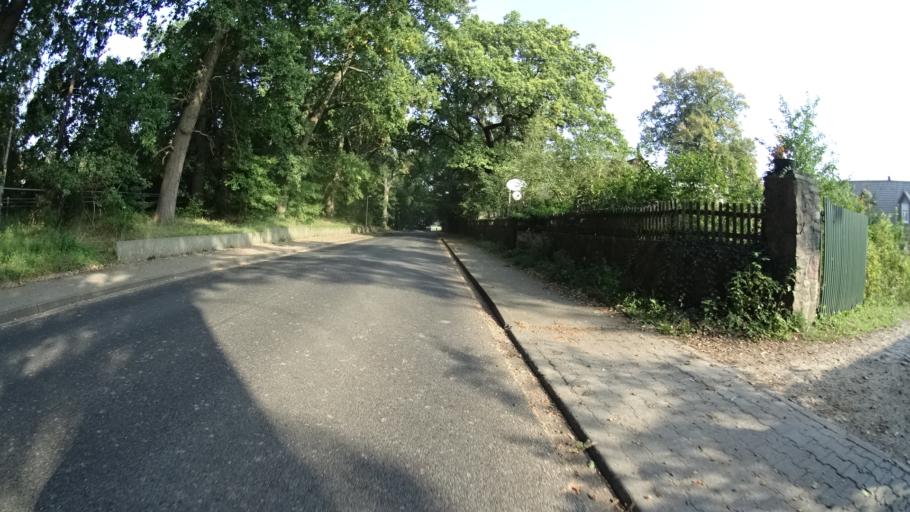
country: DE
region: Lower Saxony
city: Reppenstedt
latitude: 53.2300
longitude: 10.3791
